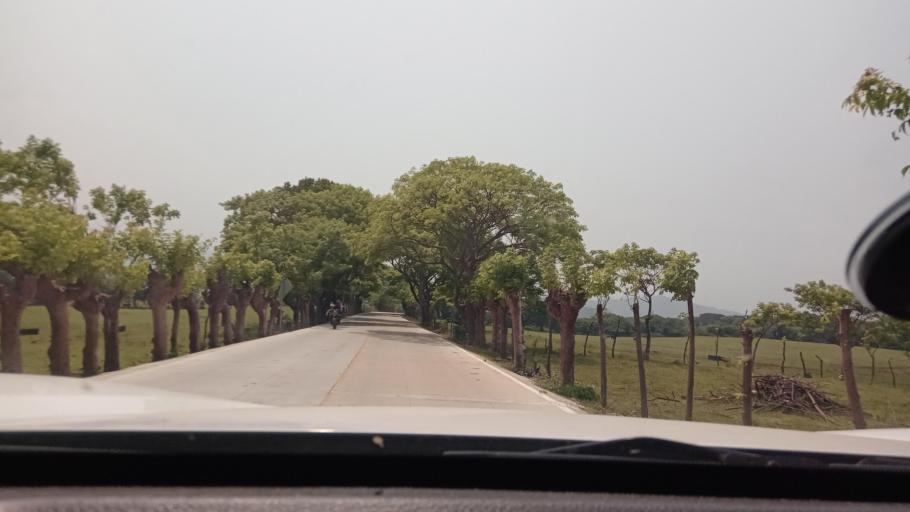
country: MX
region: Veracruz
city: Catemaco
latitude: 18.5586
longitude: -95.0199
